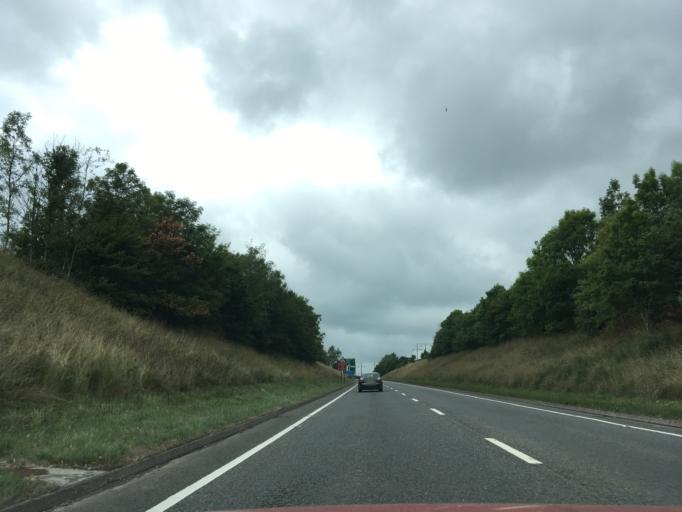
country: GB
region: Wales
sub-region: Carmarthenshire
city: Whitland
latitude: 51.8244
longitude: -4.5881
